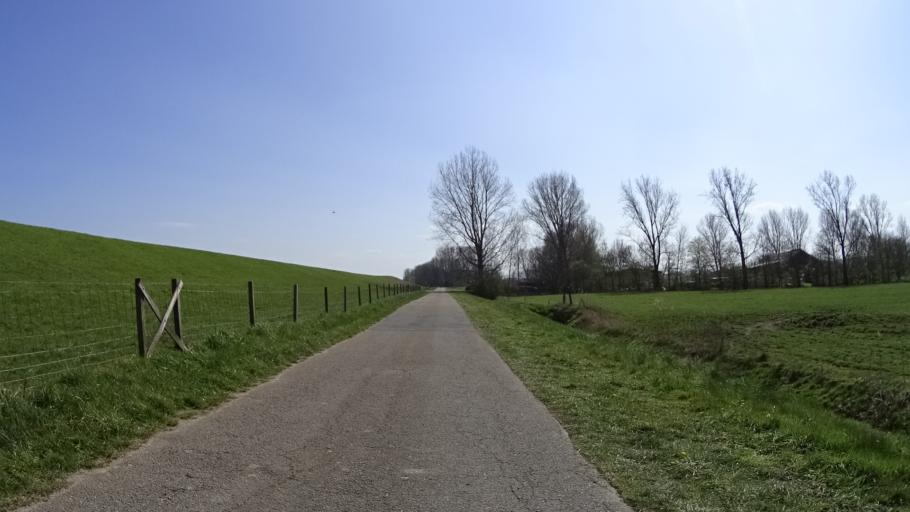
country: DE
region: Lower Saxony
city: Weener
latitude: 53.1300
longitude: 7.3639
